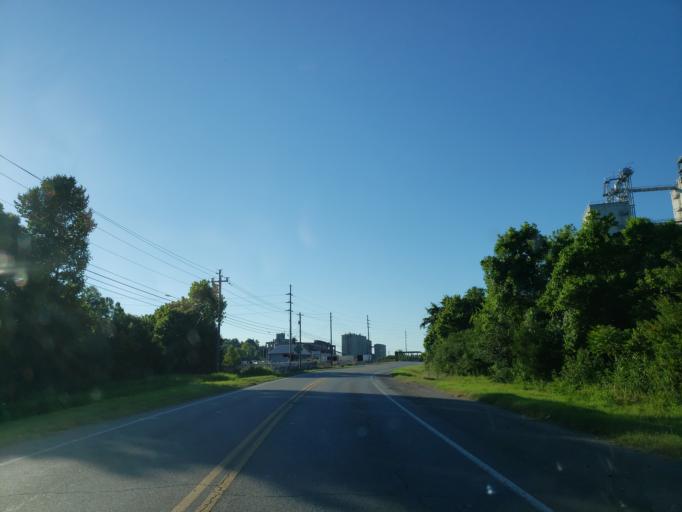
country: US
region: Georgia
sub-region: Polk County
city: Rockmart
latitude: 34.0148
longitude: -85.0472
